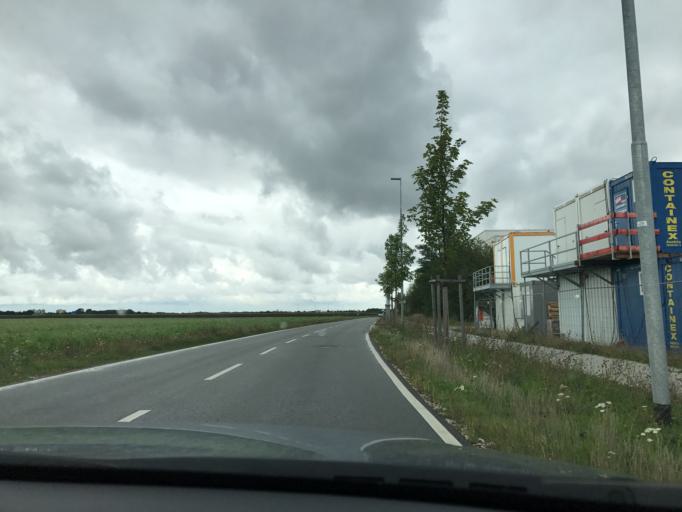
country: DE
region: Bavaria
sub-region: Upper Bavaria
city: Ottobrunn
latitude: 48.0490
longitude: 11.6516
